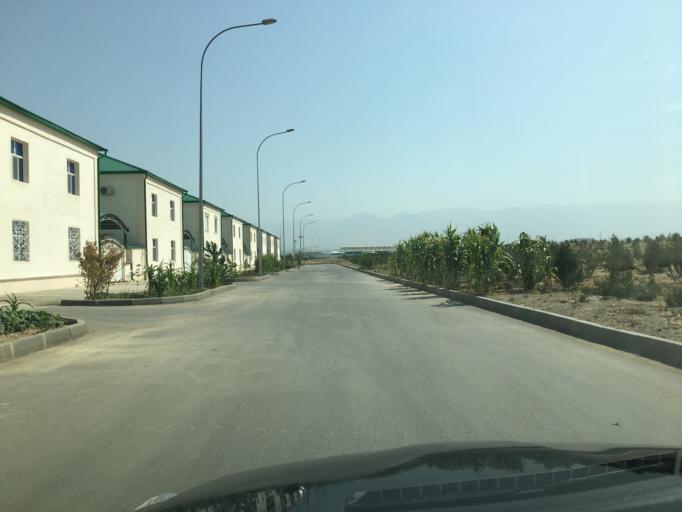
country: TM
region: Ahal
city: Ashgabat
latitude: 38.0050
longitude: 58.3954
